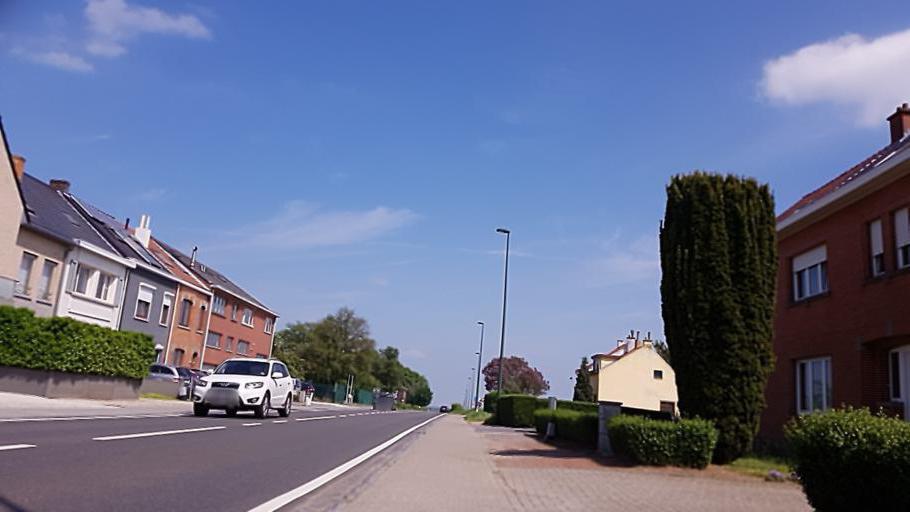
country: BE
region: Flanders
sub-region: Provincie Vlaams-Brabant
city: Steenokkerzeel
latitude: 50.8869
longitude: 4.5091
